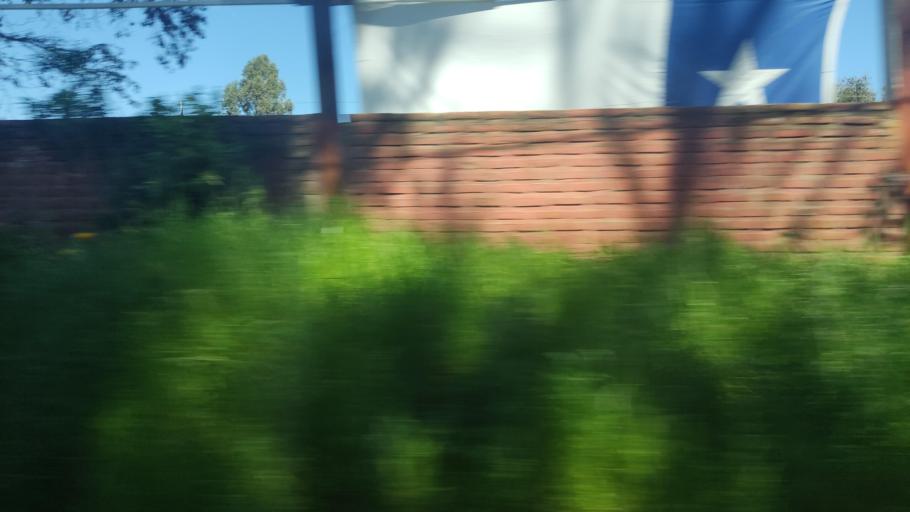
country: CL
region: Valparaiso
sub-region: Provincia de Marga Marga
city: Villa Alemana
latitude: -33.1553
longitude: -71.3310
